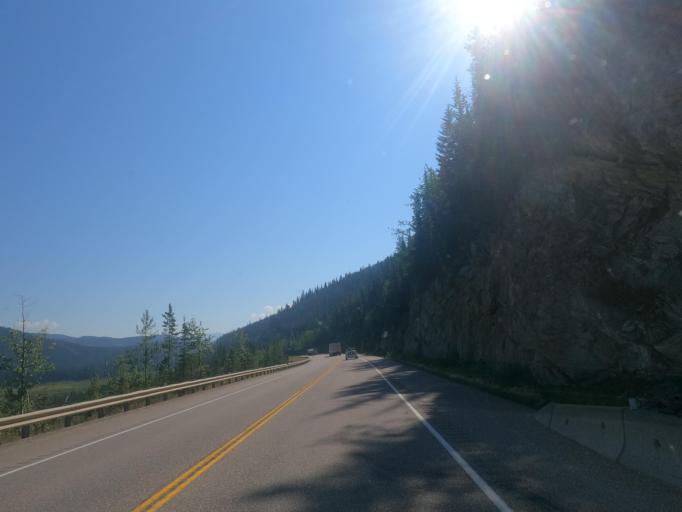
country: CA
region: Alberta
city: Jasper Park Lodge
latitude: 52.8731
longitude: -118.3040
